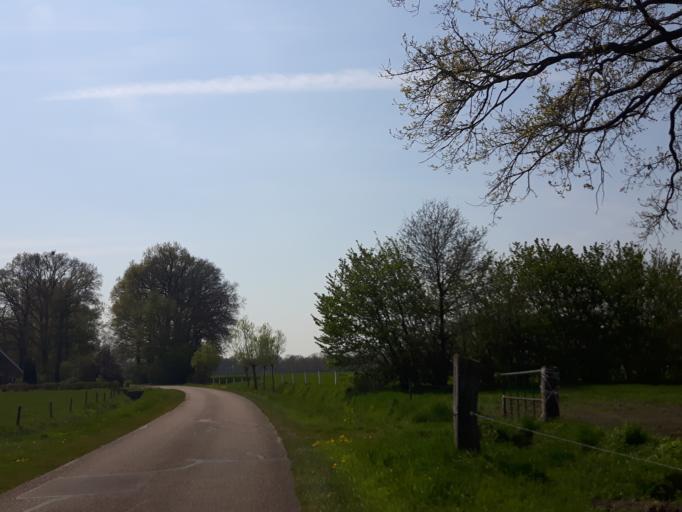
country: NL
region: Overijssel
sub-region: Gemeente Enschede
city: Enschede
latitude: 52.1405
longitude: 6.8386
